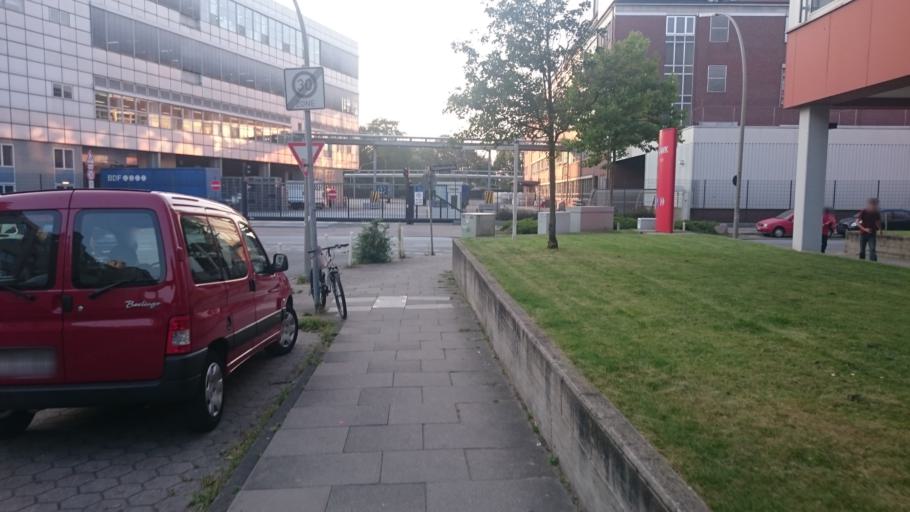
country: DE
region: Hamburg
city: Hamburg-Nord
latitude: 53.5845
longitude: 9.9646
